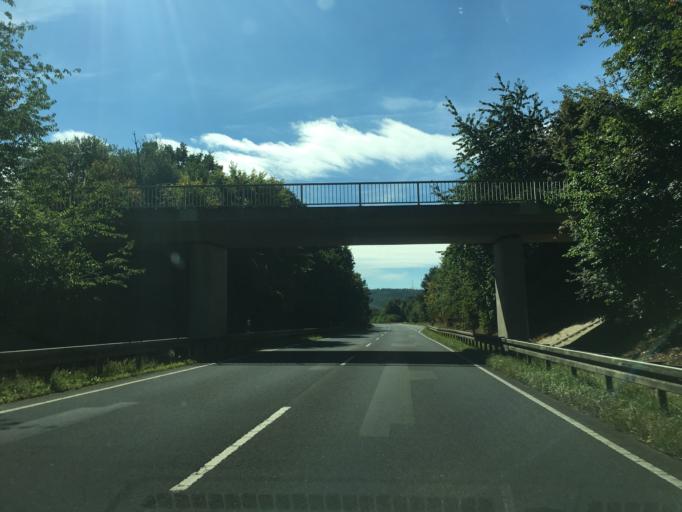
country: DE
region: Lower Saxony
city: Hameln
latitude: 52.0496
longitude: 9.3695
